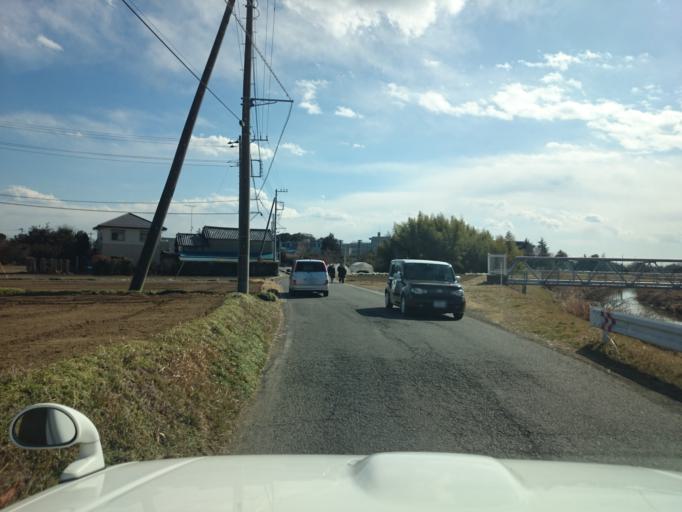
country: JP
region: Saitama
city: Kukichuo
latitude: 36.0606
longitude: 139.6991
